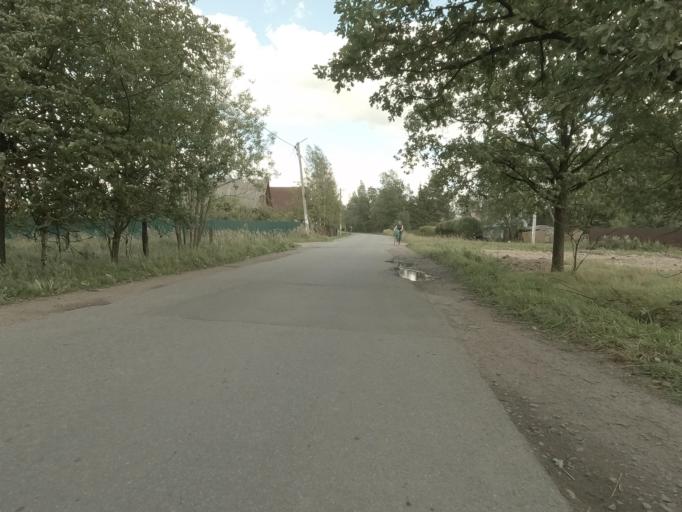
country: RU
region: Leningrad
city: Ul'yanovka
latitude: 59.6337
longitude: 30.7694
